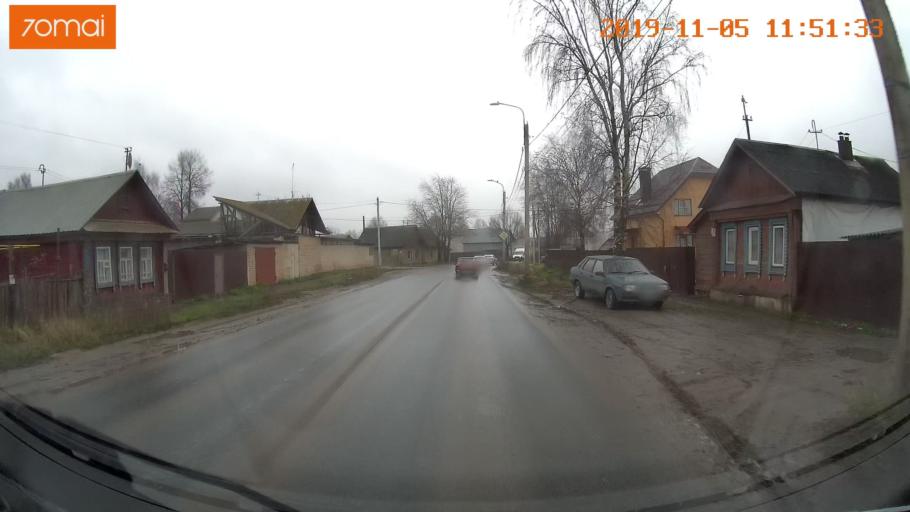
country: RU
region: Ivanovo
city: Bogorodskoye
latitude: 57.0051
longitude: 41.0280
